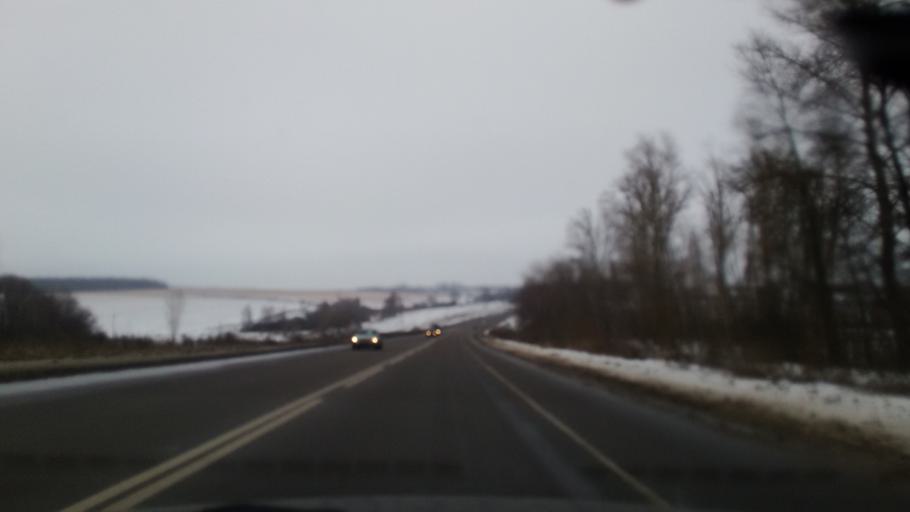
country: RU
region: Tula
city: Bolokhovo
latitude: 54.0393
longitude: 37.8702
